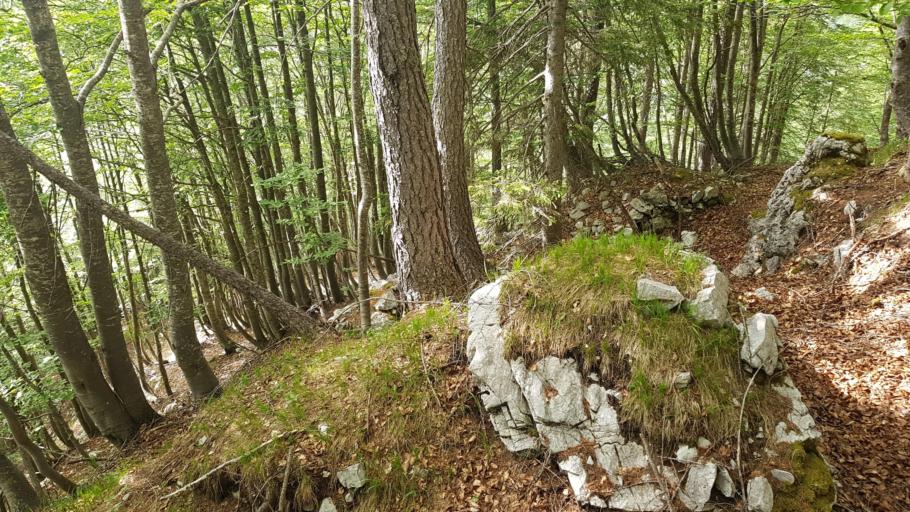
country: IT
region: Friuli Venezia Giulia
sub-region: Provincia di Udine
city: Pontebba
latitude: 46.5344
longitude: 13.2781
